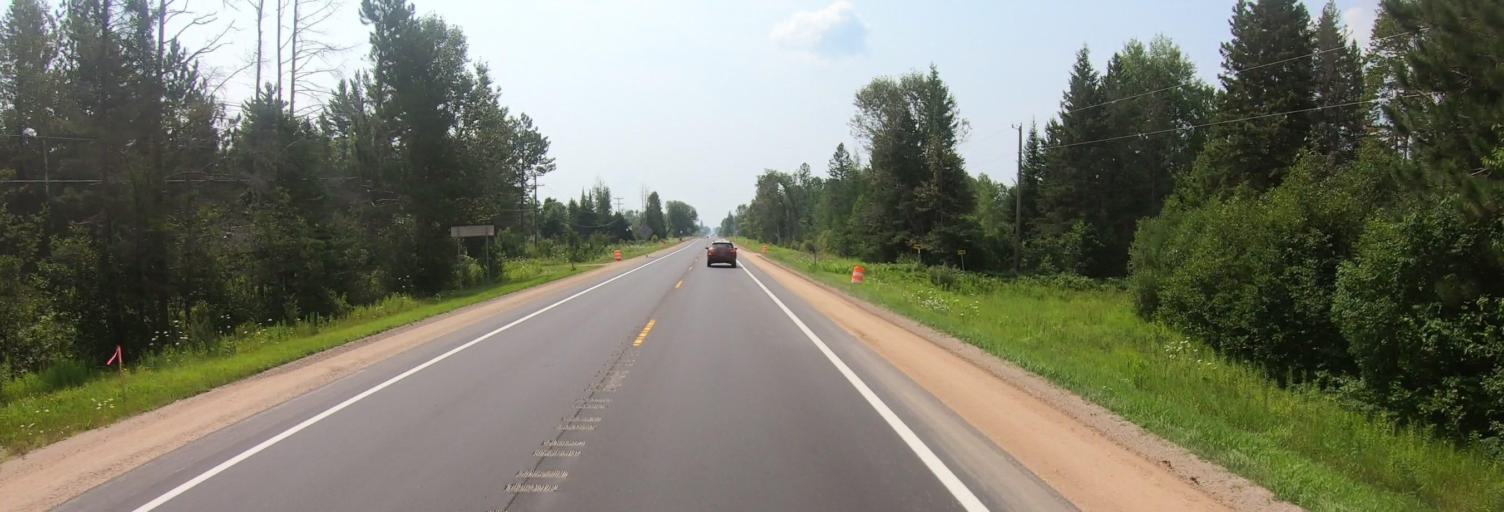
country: US
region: Michigan
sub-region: Luce County
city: Newberry
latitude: 46.3688
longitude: -85.5099
